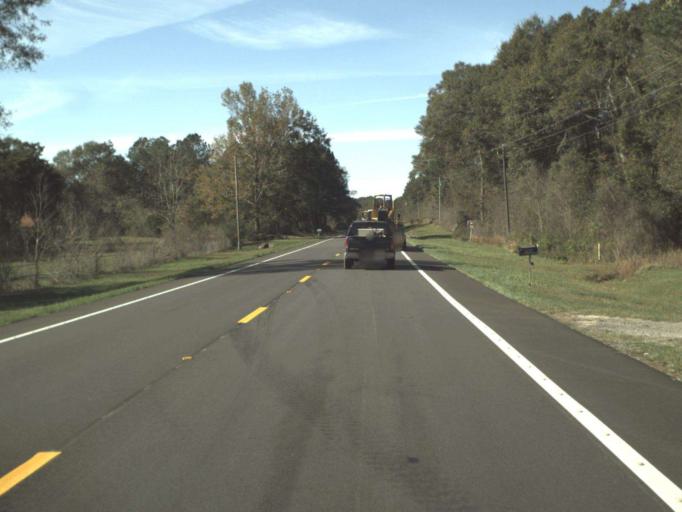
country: US
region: Alabama
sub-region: Escambia County
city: East Brewton
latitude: 30.8952
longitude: -86.9875
